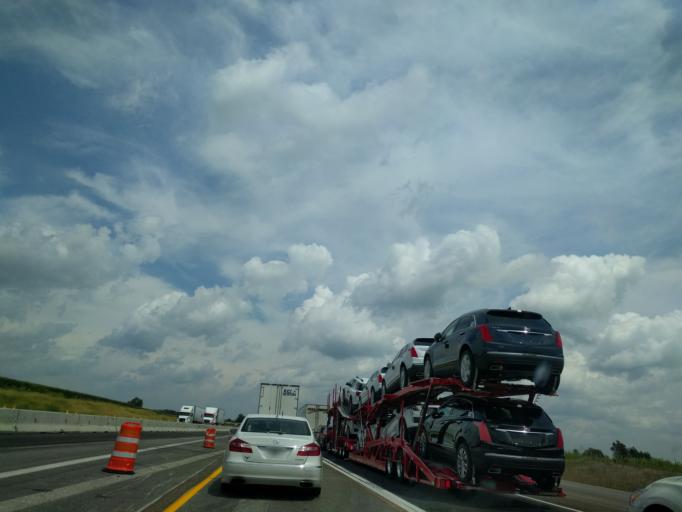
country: US
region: Kentucky
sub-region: Larue County
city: Hodgenville
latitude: 37.5487
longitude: -85.8790
